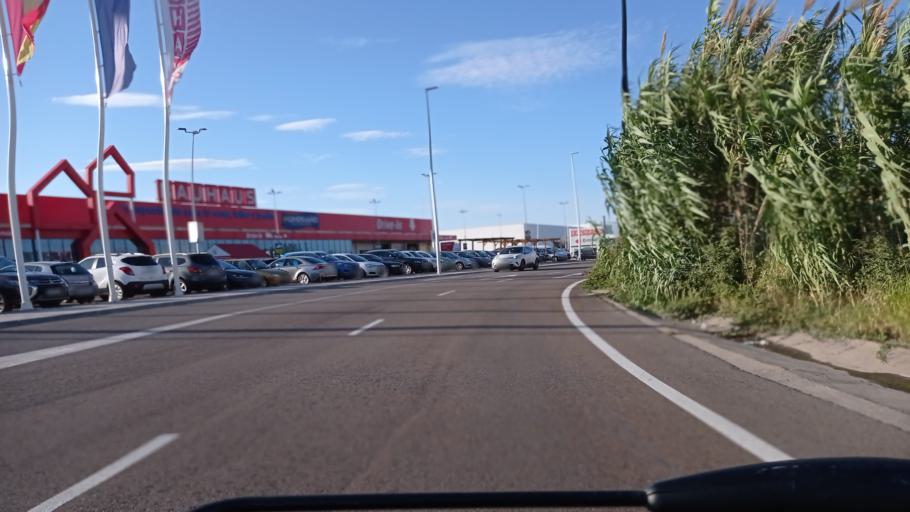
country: ES
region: Aragon
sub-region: Provincia de Zaragoza
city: Oliver-Valdefierro, Oliver, Valdefierro
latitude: 41.6743
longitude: -0.9505
